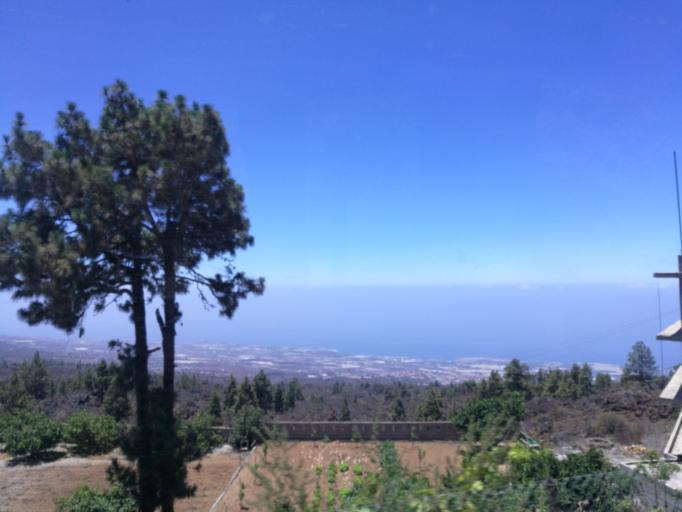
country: ES
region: Canary Islands
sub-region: Provincia de Santa Cruz de Tenerife
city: Guia de Isora
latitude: 28.2290
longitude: -16.7591
